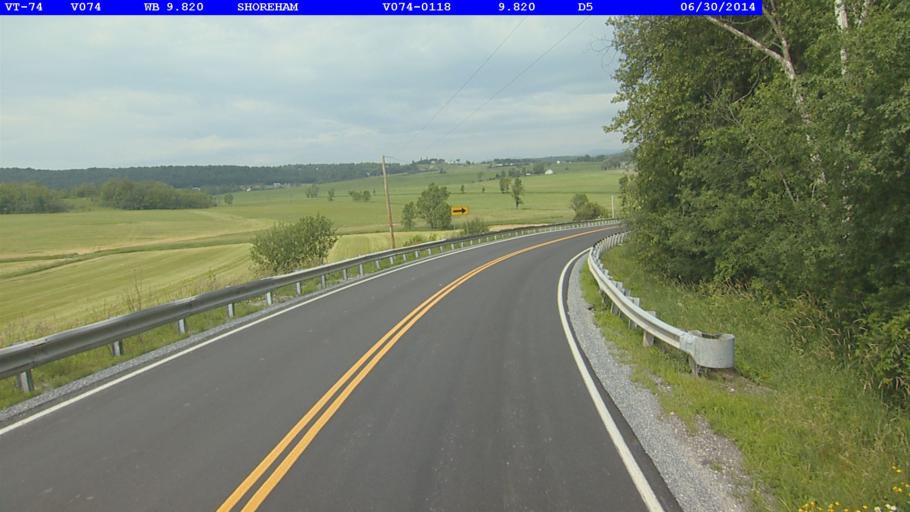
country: US
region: Vermont
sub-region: Addison County
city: Middlebury (village)
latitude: 43.9415
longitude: -73.2592
